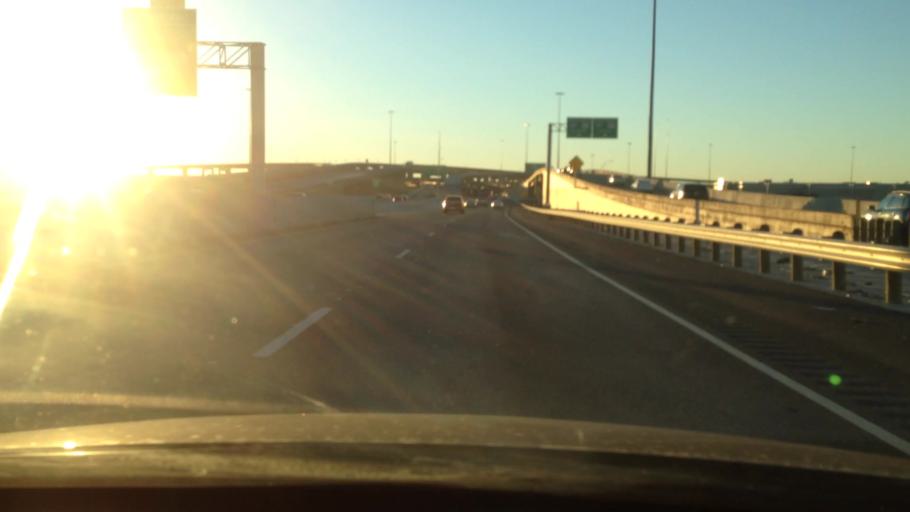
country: US
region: Texas
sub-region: Tarrant County
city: Blue Mound
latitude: 32.8397
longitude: -97.3025
